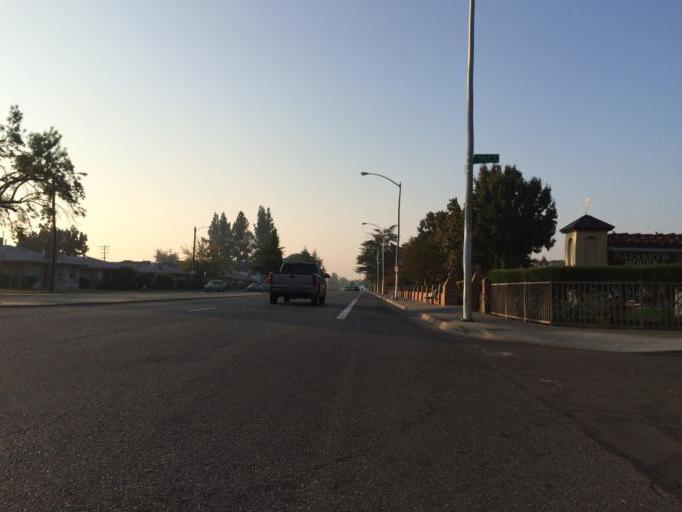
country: US
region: California
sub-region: Fresno County
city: Fresno
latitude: 36.7706
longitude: -119.7727
